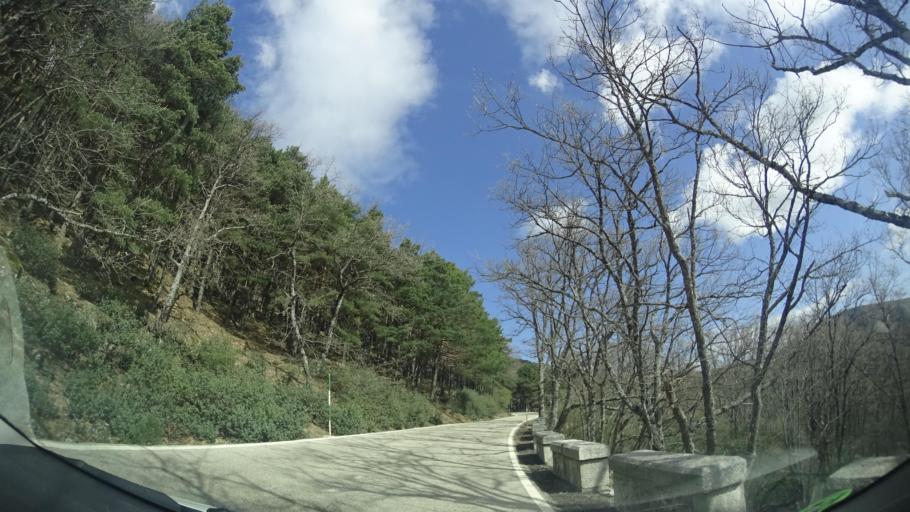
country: ES
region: Madrid
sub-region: Provincia de Madrid
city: Miraflores de la Sierra
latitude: 40.8509
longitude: -3.7660
